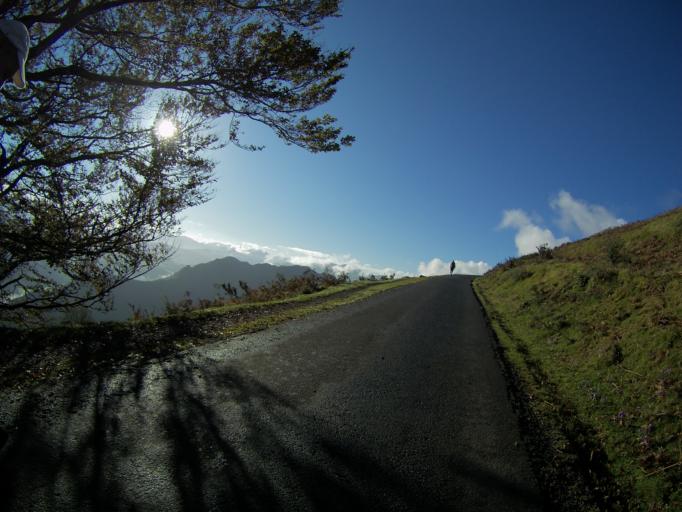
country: FR
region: Aquitaine
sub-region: Departement des Pyrenees-Atlantiques
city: Saint-Jean-Pied-de-Port
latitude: 43.1134
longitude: -1.2375
